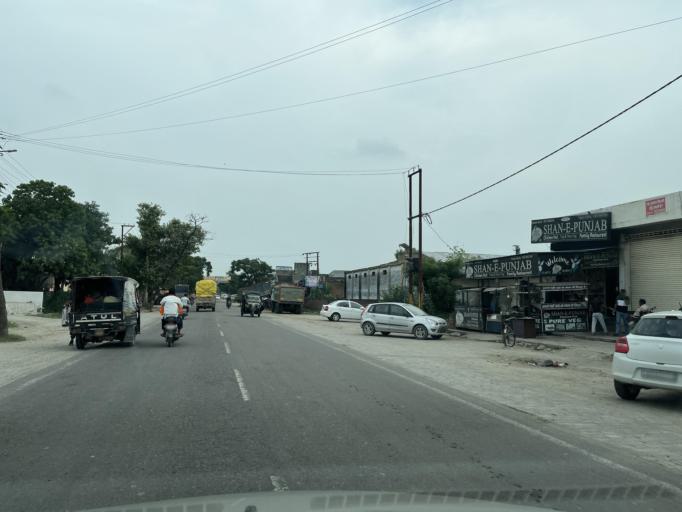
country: IN
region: Uttar Pradesh
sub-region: Rampur
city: Bilaspur
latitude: 29.0380
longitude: 79.2534
